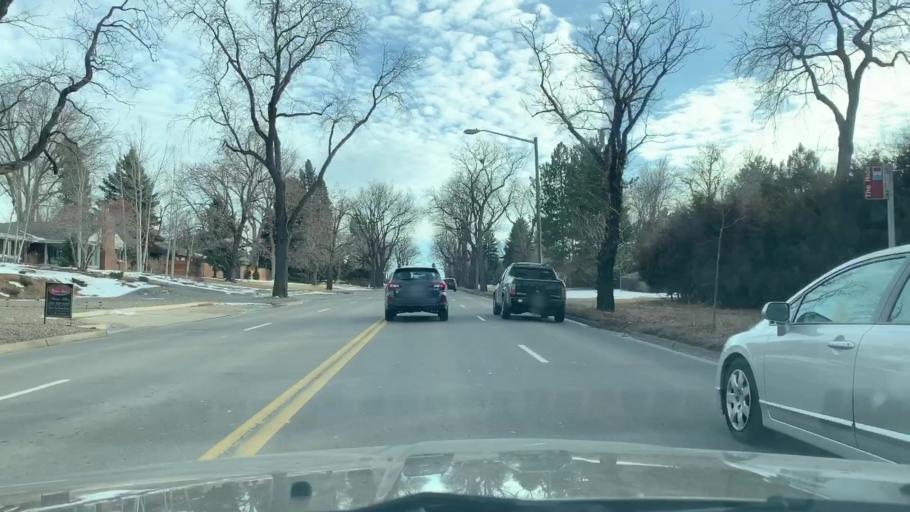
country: US
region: Colorado
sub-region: Arapahoe County
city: Glendale
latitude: 39.7215
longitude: -104.9128
